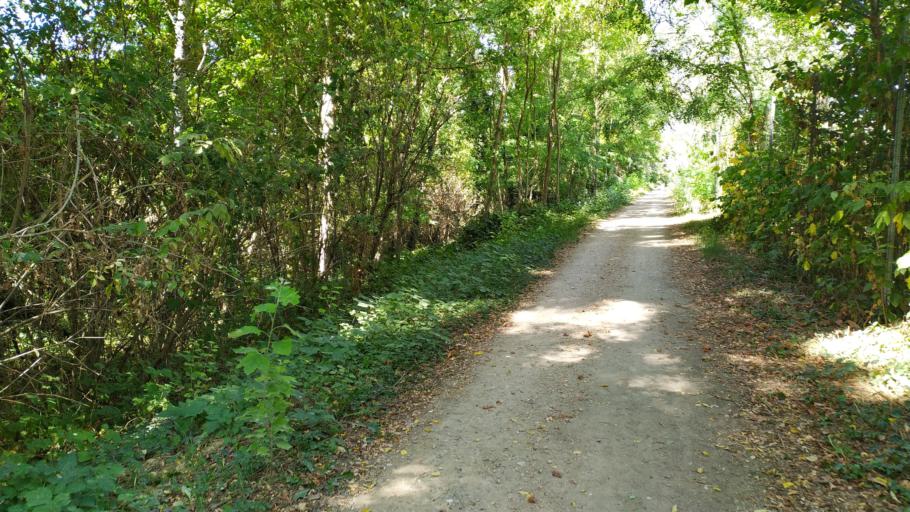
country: IT
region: Emilia-Romagna
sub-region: Forli-Cesena
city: Forli
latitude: 44.2035
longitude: 12.0071
